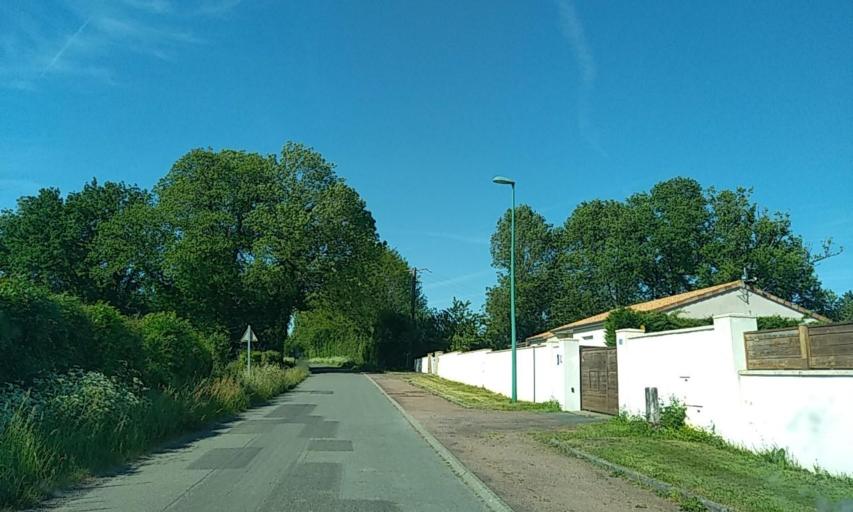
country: FR
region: Poitou-Charentes
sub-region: Departement des Deux-Sevres
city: Boisme
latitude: 46.7794
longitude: -0.4278
